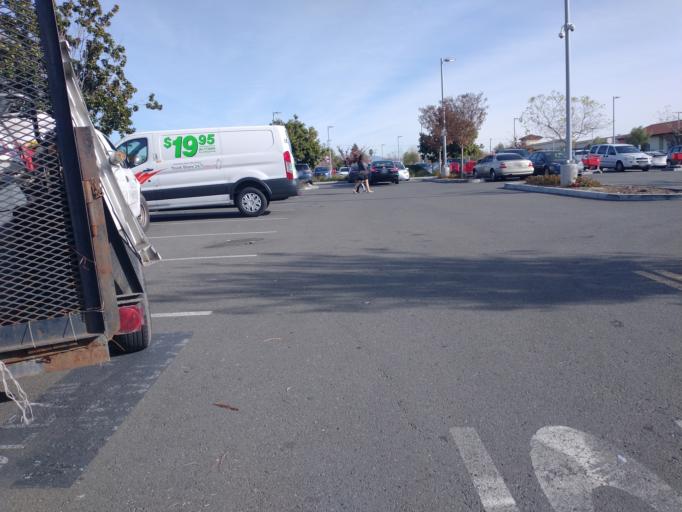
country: US
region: California
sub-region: Santa Clara County
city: Santa Clara
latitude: 37.3509
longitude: -121.9618
